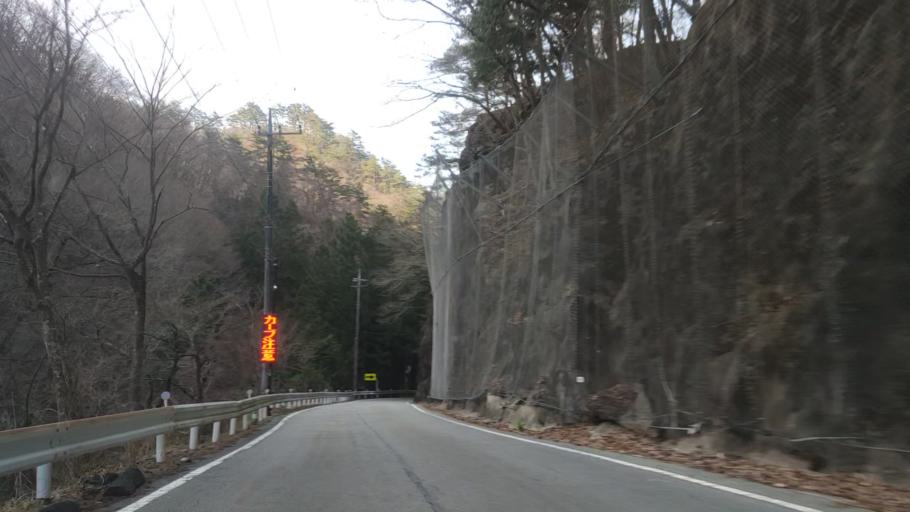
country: JP
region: Yamanashi
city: Fujikawaguchiko
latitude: 35.5348
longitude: 138.6238
